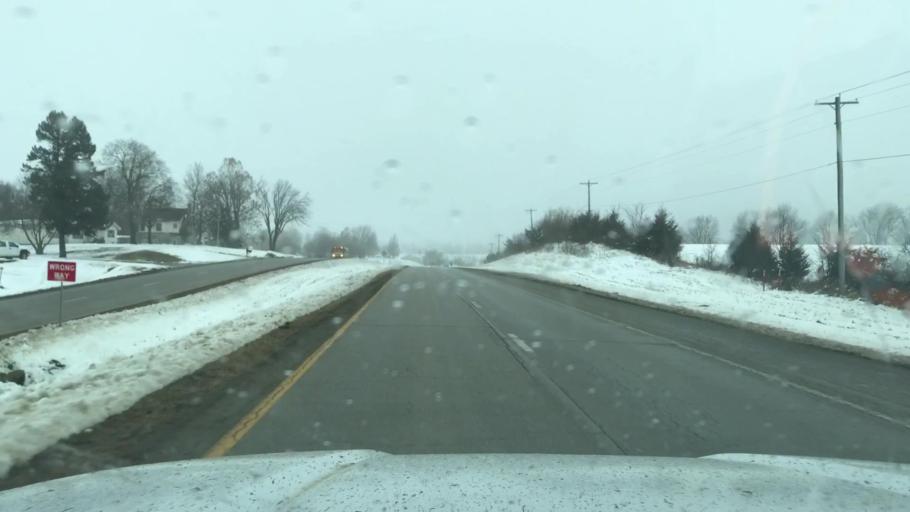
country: US
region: Missouri
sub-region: Andrew County
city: Country Club Village
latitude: 39.8707
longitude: -94.8087
